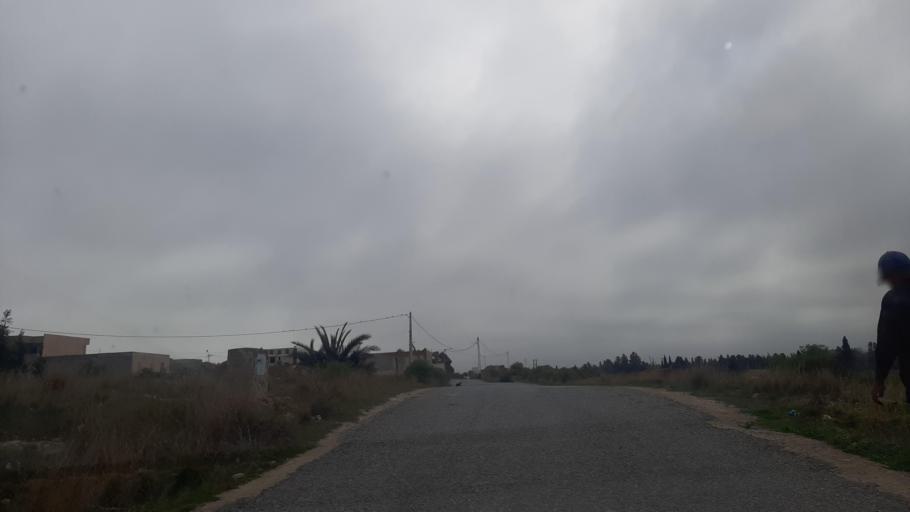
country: TN
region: Nabul
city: Menzel Heurr
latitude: 36.6729
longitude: 10.9196
